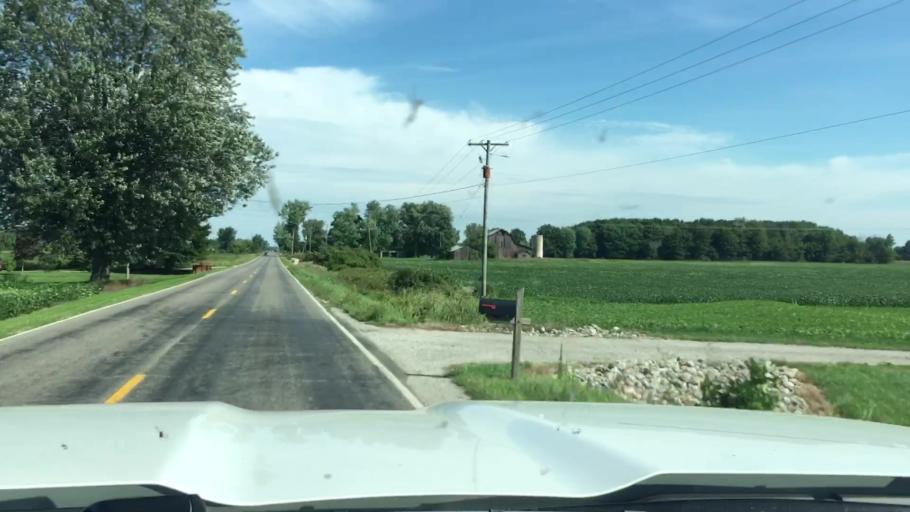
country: US
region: Michigan
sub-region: Saginaw County
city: Hemlock
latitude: 43.4879
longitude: -84.2299
